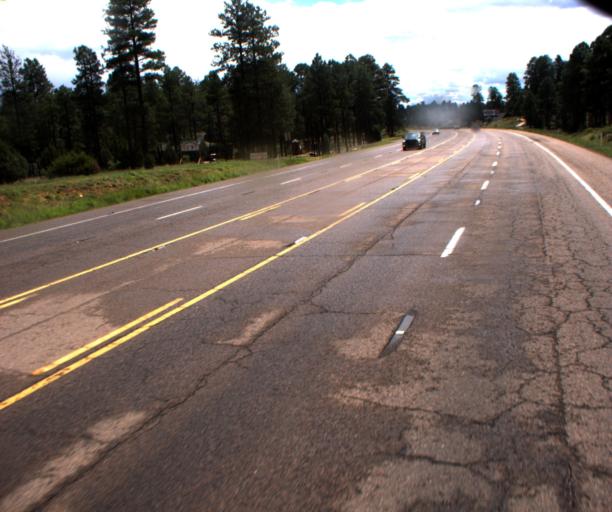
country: US
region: Arizona
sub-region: Navajo County
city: Heber-Overgaard
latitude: 34.3935
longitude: -110.5569
